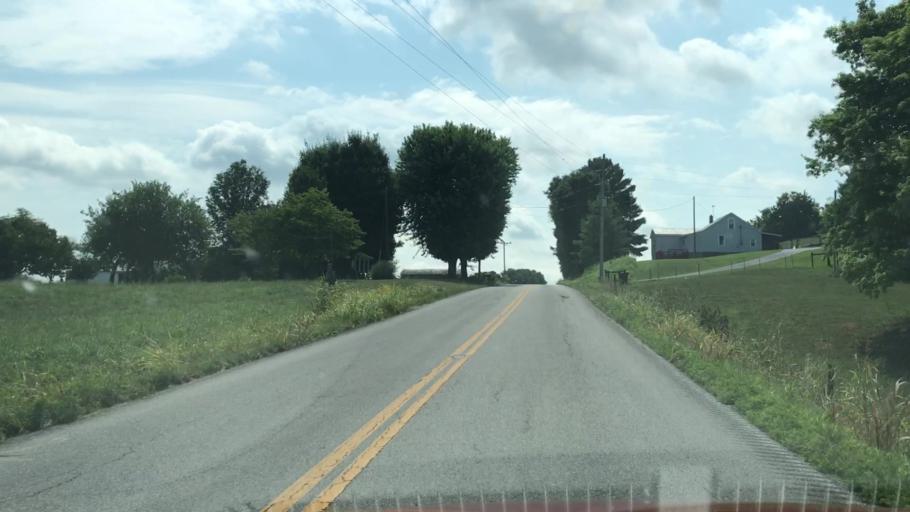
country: US
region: Kentucky
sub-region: Barren County
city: Glasgow
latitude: 36.8408
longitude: -85.8331
